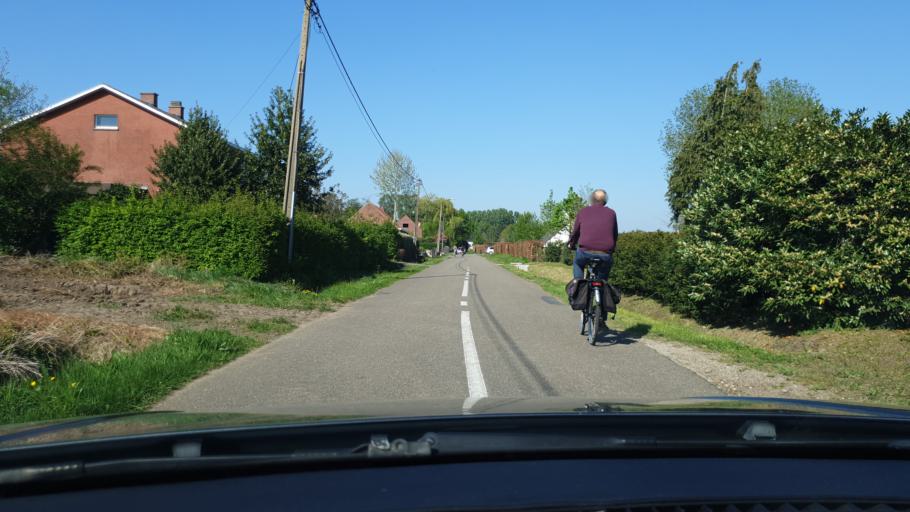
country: BE
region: Flanders
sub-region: Provincie Antwerpen
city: Geel
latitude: 51.1430
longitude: 4.9743
